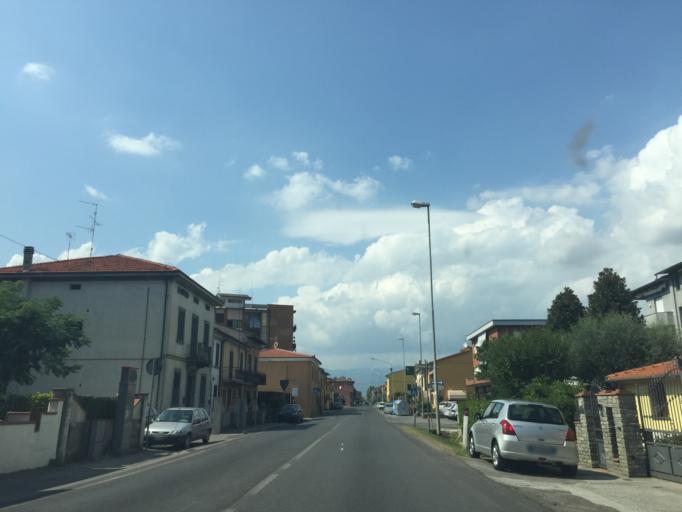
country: IT
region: Tuscany
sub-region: Provincia di Pistoia
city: Barba
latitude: 43.8899
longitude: 10.9625
